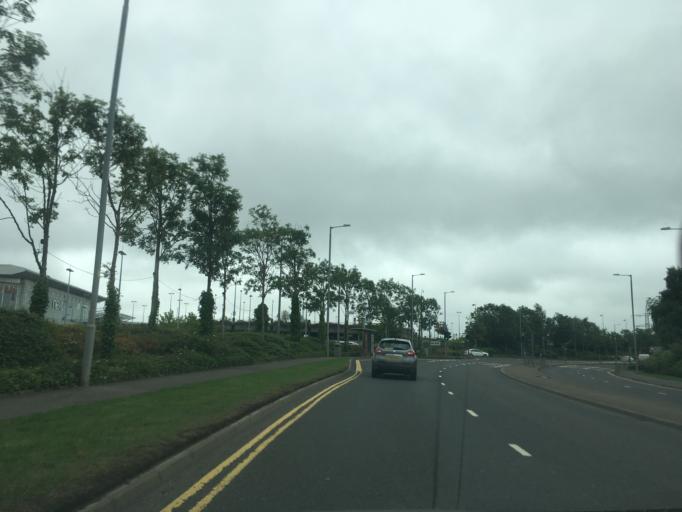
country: GB
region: Scotland
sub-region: Renfrewshire
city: Renfrew
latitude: 55.8763
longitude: -4.3692
